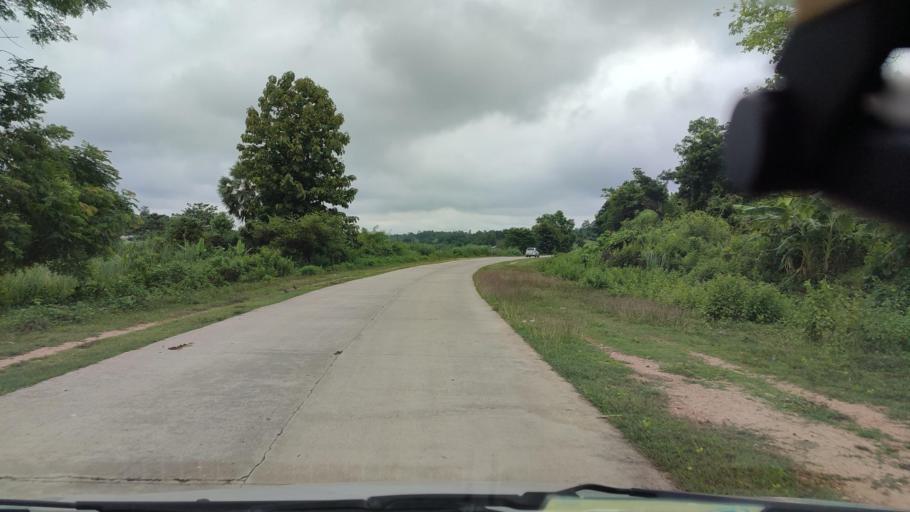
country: MM
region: Mandalay
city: Nay Pyi Taw
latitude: 19.9382
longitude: 95.9774
